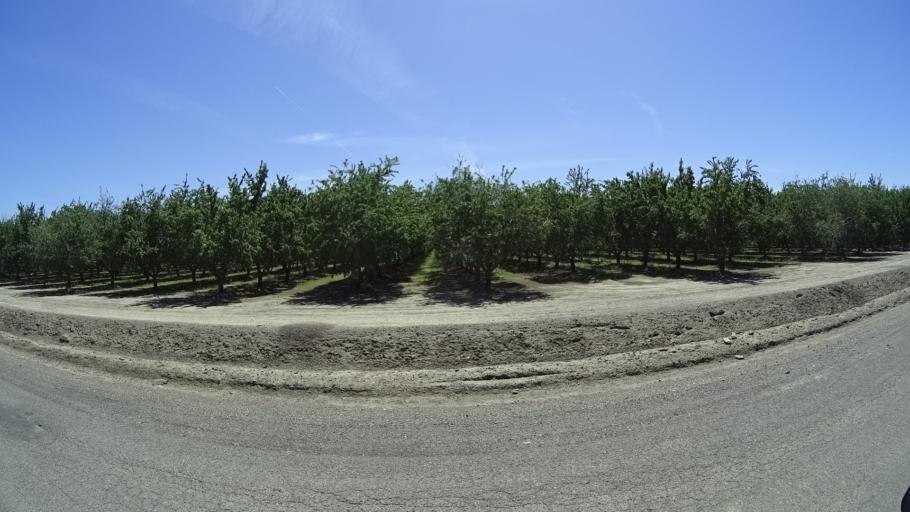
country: US
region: California
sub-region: Glenn County
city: Orland
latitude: 39.7323
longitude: -122.1340
